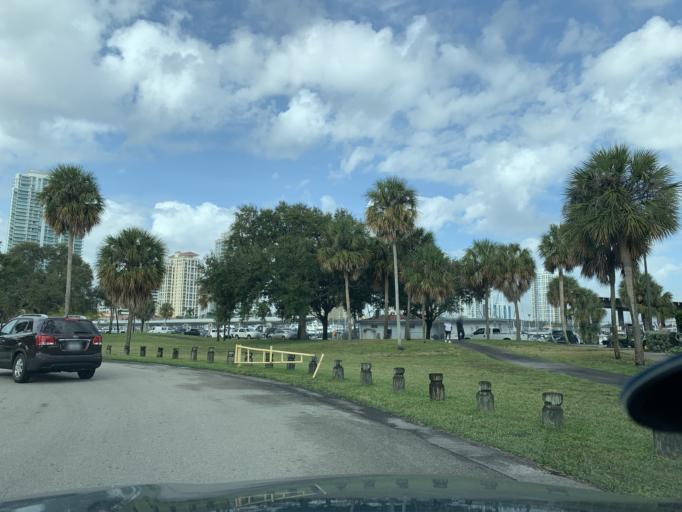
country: US
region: Florida
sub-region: Pinellas County
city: Saint Petersburg
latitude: 27.7702
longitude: -82.6289
